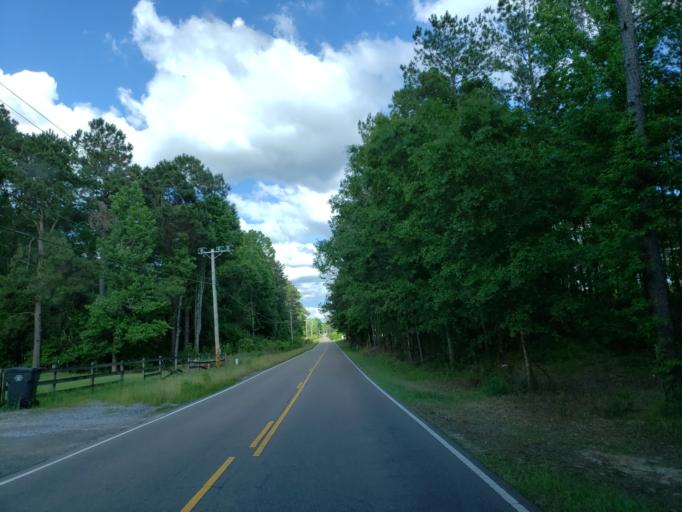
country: US
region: Mississippi
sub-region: Lamar County
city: West Hattiesburg
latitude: 31.2737
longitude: -89.3765
